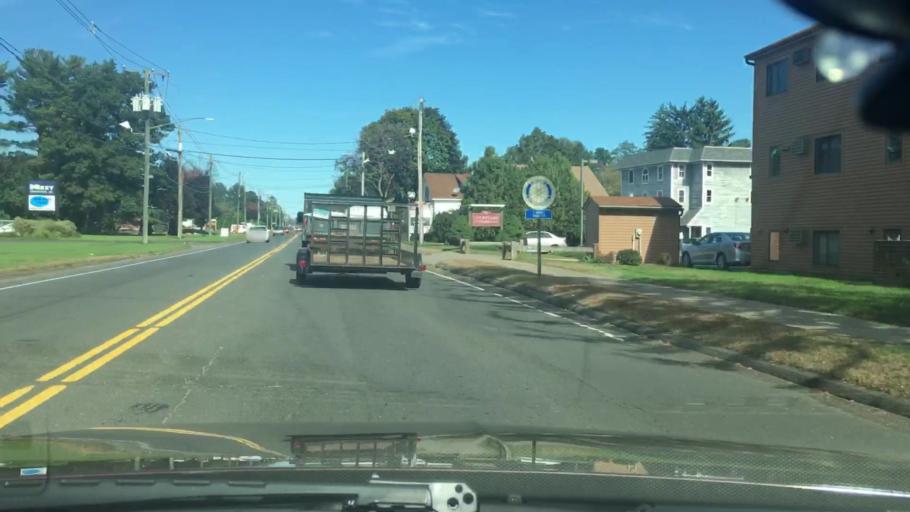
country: US
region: Connecticut
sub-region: Hartford County
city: Plainville
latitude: 41.6511
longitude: -72.8704
